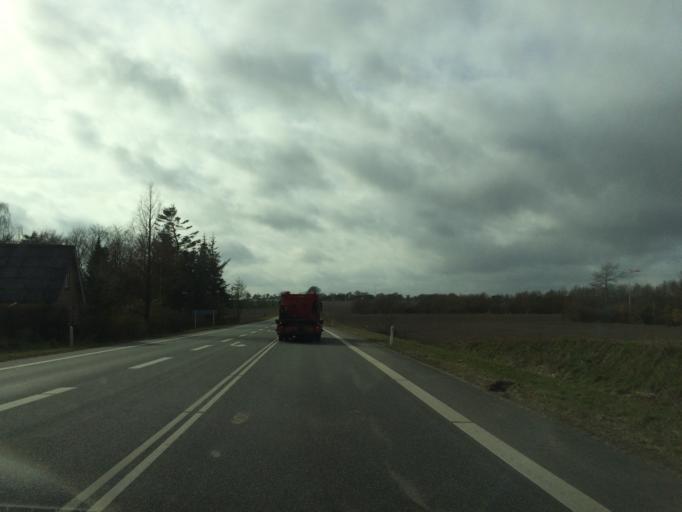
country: DK
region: Central Jutland
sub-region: Randers Kommune
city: Langa
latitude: 56.4778
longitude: 9.9104
